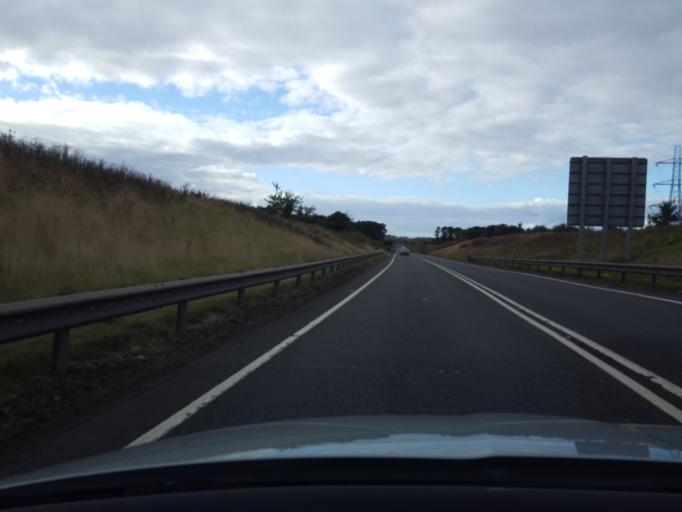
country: GB
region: Scotland
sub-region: Midlothian
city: Dalkeith
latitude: 55.9112
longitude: -3.0490
